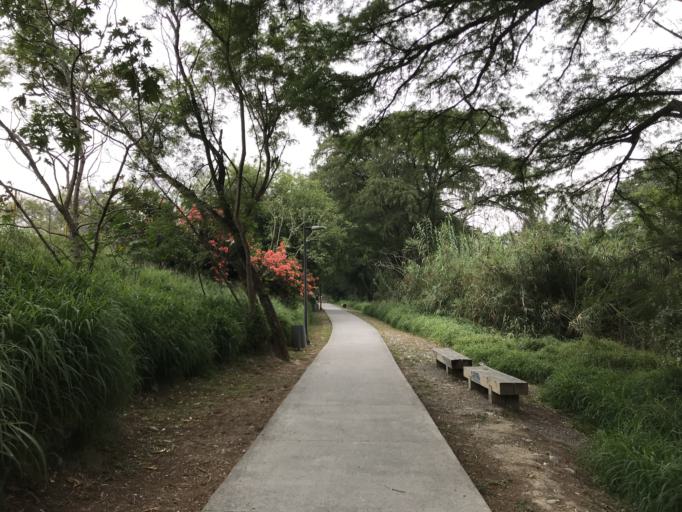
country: MX
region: Nuevo Leon
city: Guadalupe
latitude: 25.6716
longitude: -100.2470
